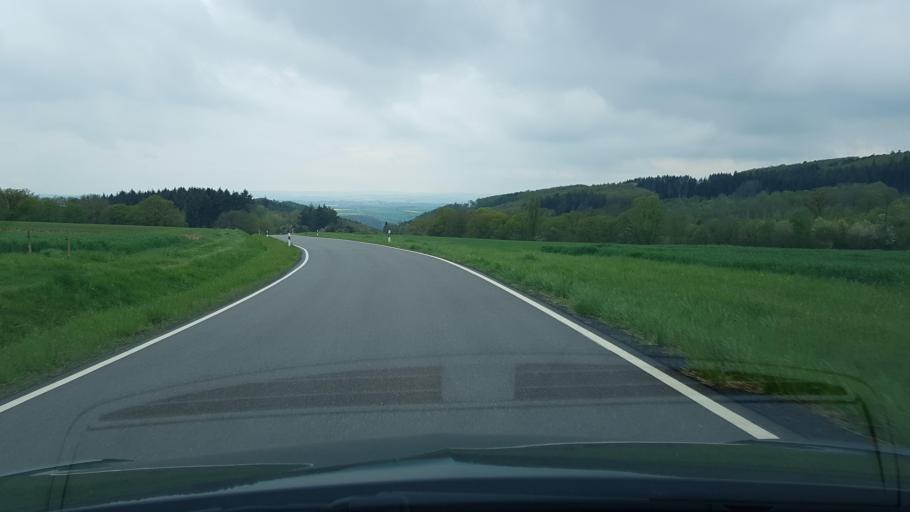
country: DE
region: Rheinland-Pfalz
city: Alken
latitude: 50.2505
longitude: 7.4817
